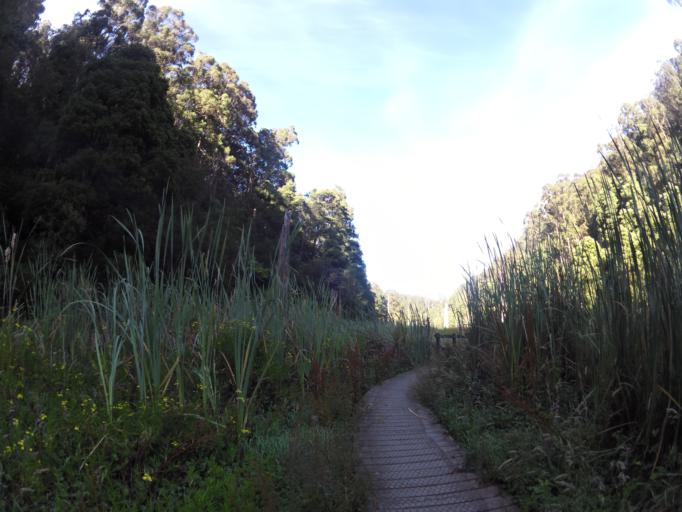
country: AU
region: Victoria
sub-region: Colac-Otway
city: Apollo Bay
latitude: -38.5524
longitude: 143.7635
